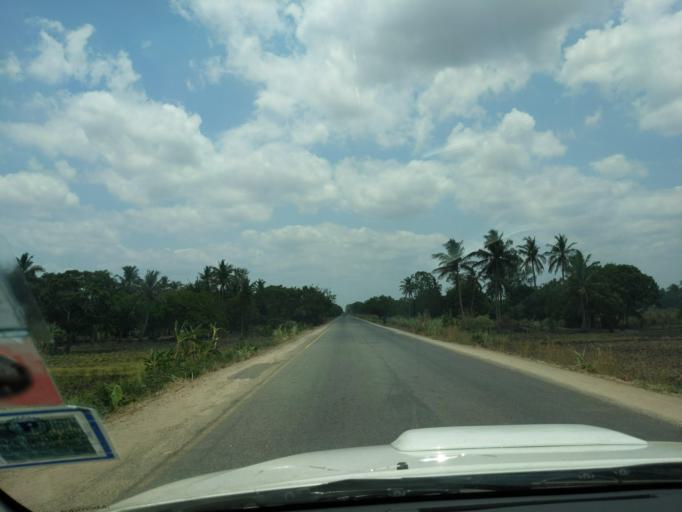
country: MZ
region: Zambezia
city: Quelimane
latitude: -17.6236
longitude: 36.8322
